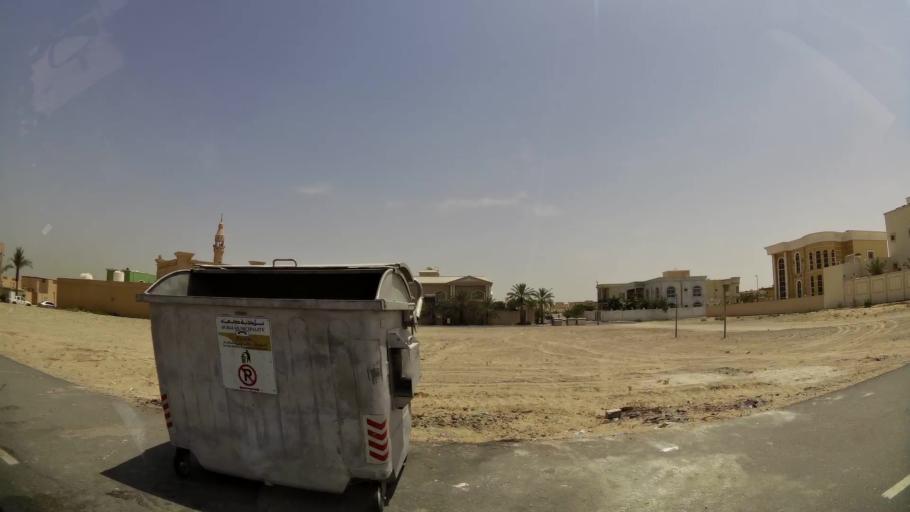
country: AE
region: Ash Shariqah
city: Sharjah
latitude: 25.1930
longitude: 55.4146
